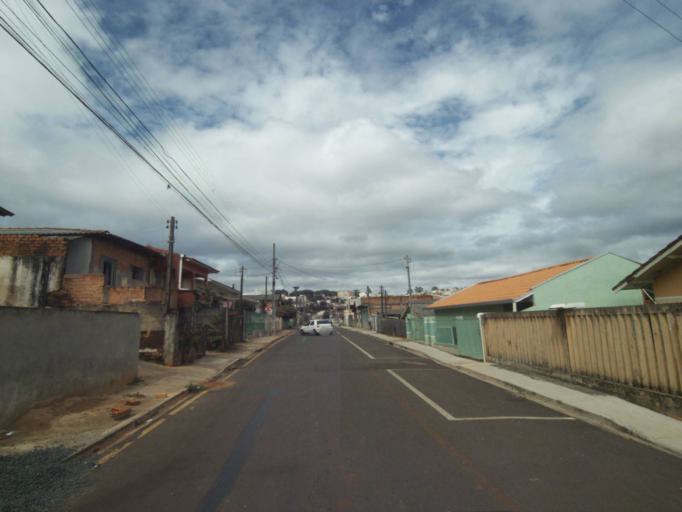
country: BR
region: Parana
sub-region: Telemaco Borba
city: Telemaco Borba
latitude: -24.3308
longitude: -50.6354
